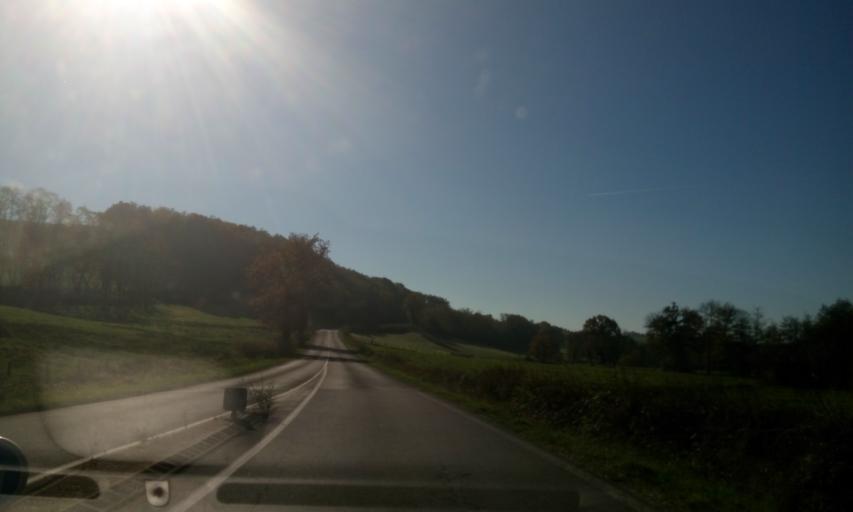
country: FR
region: Rhone-Alpes
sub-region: Departement du Rhone
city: Bourg-de-Thizy
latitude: 46.0162
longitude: 4.2713
